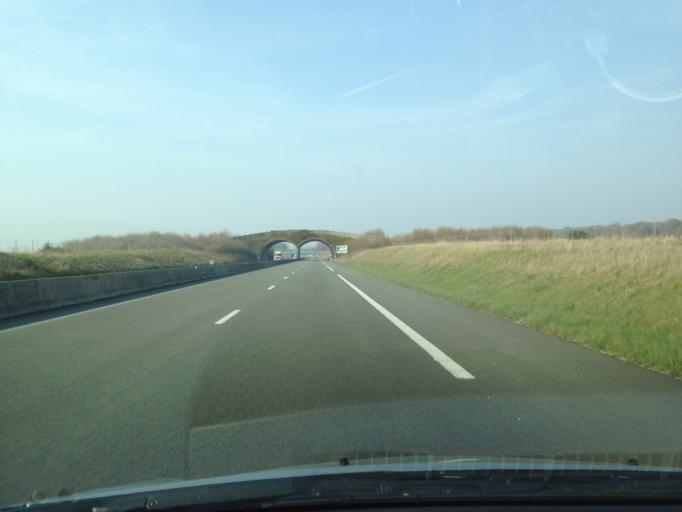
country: FR
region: Picardie
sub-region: Departement de la Somme
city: Nouvion
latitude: 50.2292
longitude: 1.7521
